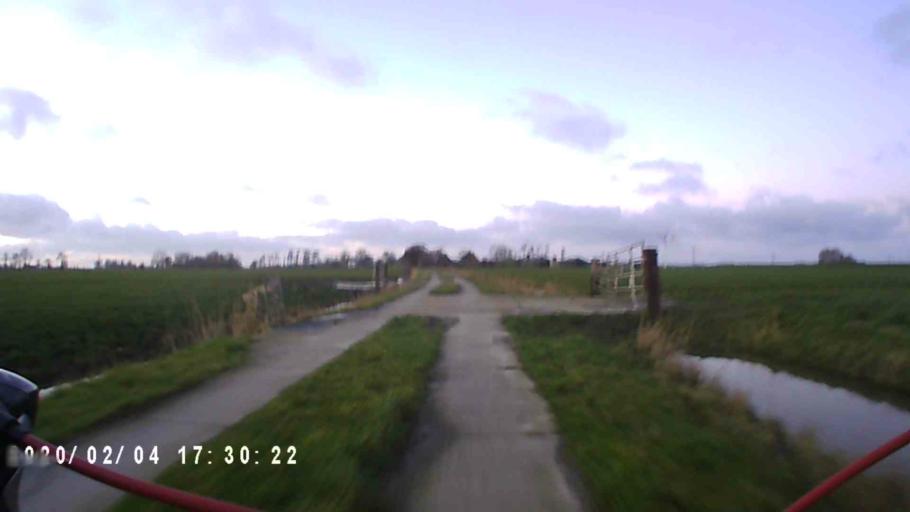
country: NL
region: Groningen
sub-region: Gemeente Zuidhorn
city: Aduard
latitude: 53.2749
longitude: 6.5016
